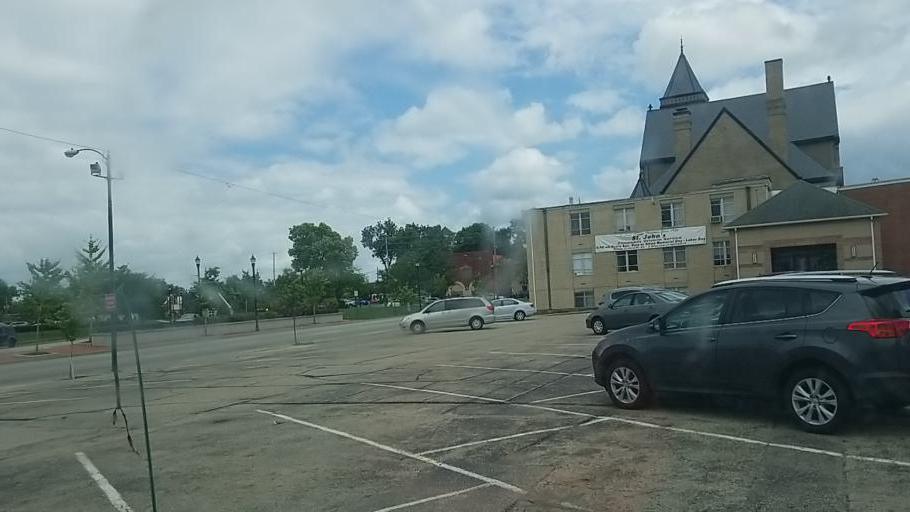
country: US
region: Ohio
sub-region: Clark County
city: Springfield
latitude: 39.9259
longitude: -83.8156
